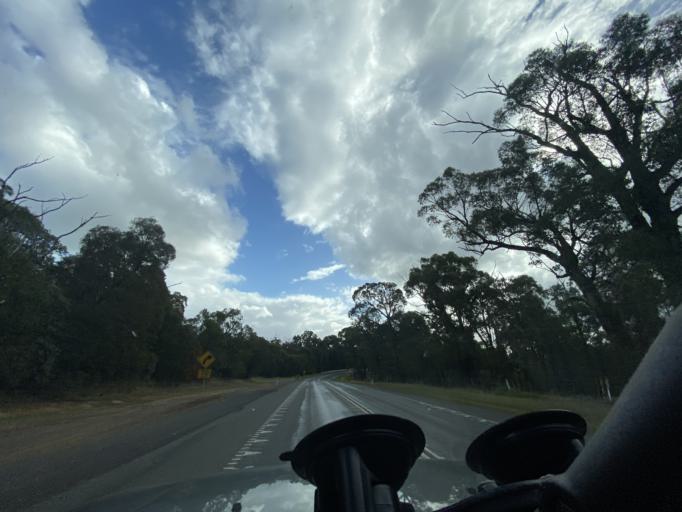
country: AU
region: Victoria
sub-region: Murrindindi
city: Kinglake West
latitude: -37.4905
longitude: 145.2166
